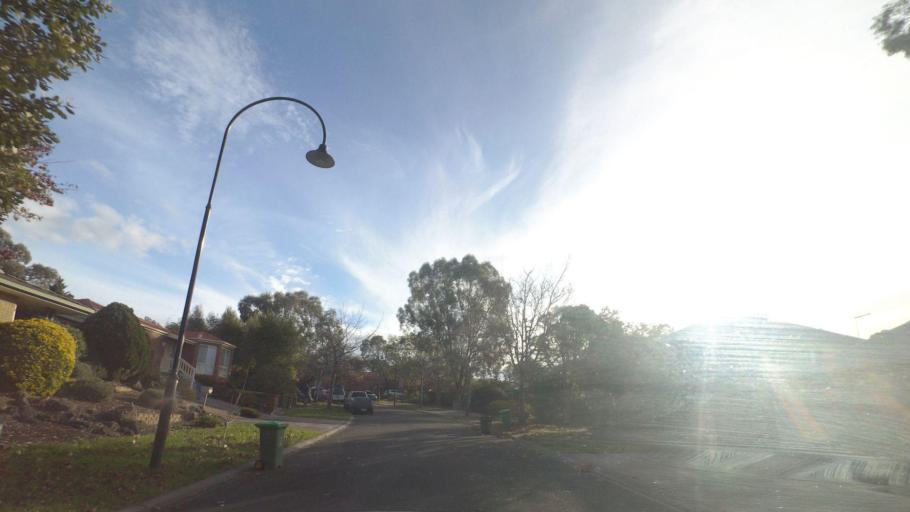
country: AU
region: Victoria
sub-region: Banyule
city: Yallambie
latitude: -37.7267
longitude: 145.0977
